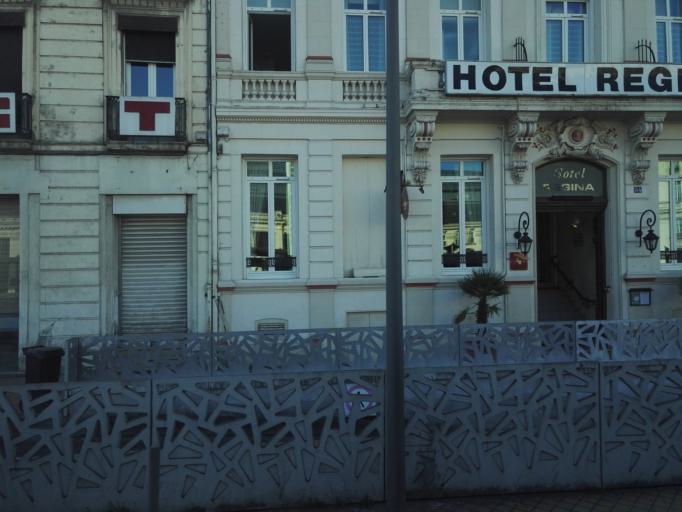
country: FR
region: Aquitaine
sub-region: Departement de la Gironde
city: Begles
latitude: 44.8253
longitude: -0.5573
